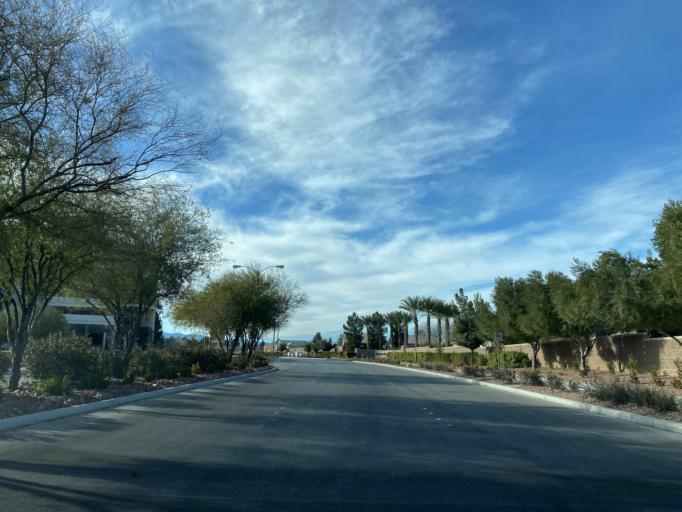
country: US
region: Nevada
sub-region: Clark County
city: North Las Vegas
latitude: 36.2942
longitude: -115.1766
